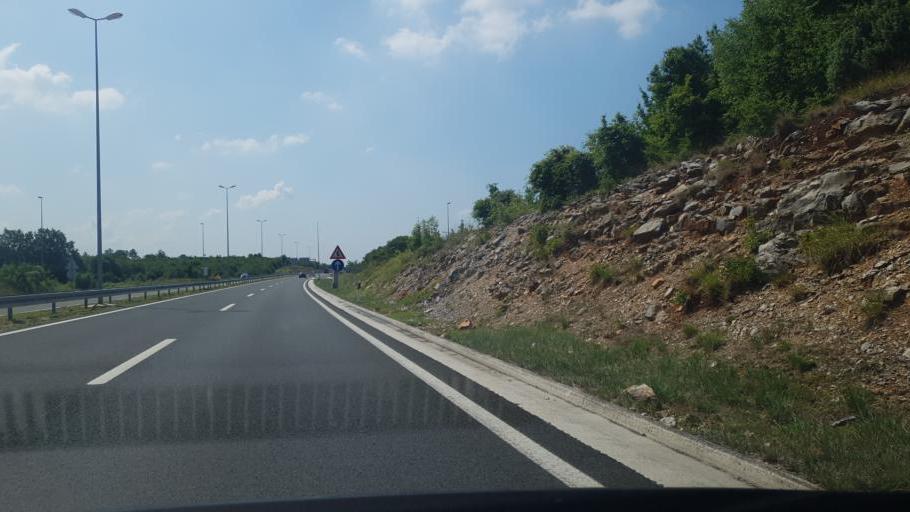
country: HR
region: Istarska
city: Vodnjan
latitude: 45.1106
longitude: 13.8156
